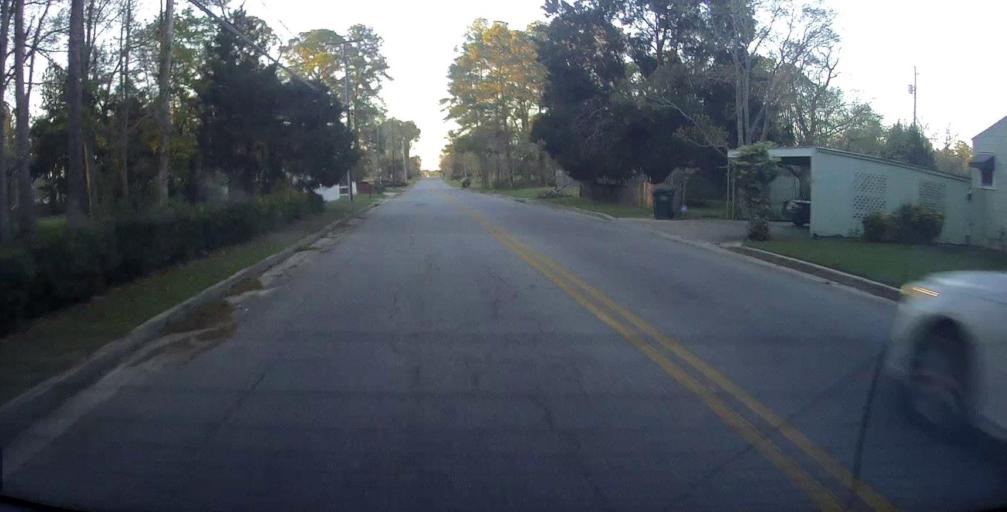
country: US
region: Georgia
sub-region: Crisp County
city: Cordele
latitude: 31.9566
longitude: -83.7656
